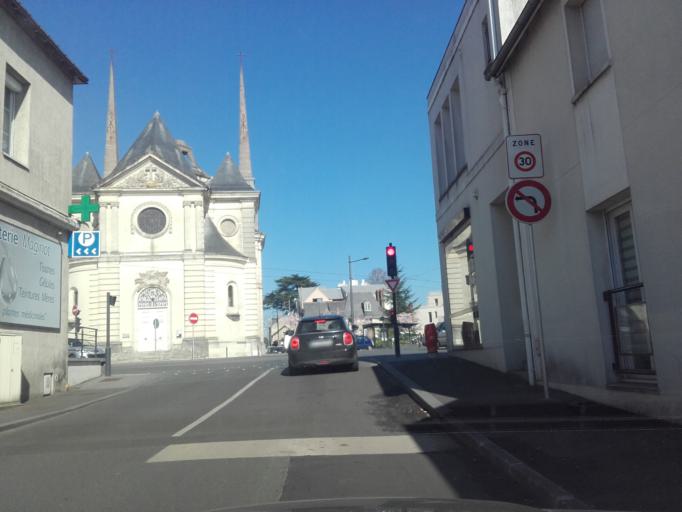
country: FR
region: Centre
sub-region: Departement d'Indre-et-Loire
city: Saint-Cyr-sur-Loire
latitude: 47.4117
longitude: 0.6848
